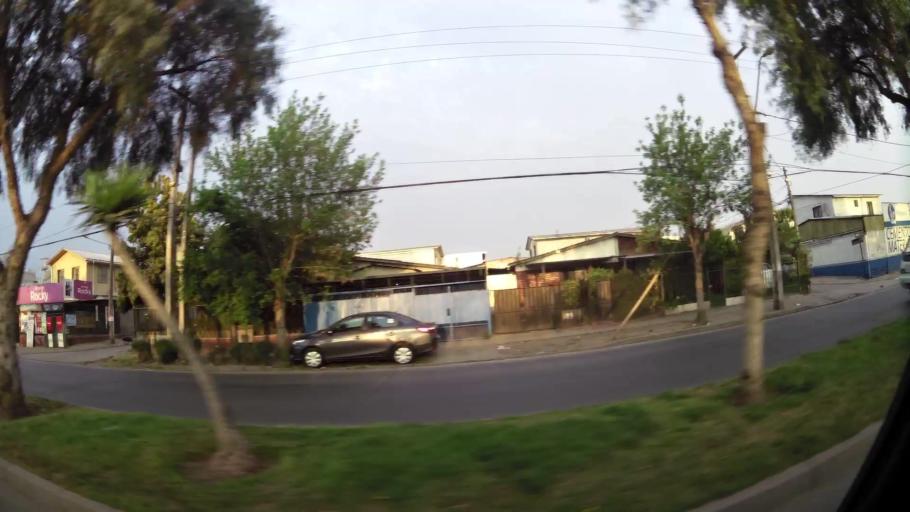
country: CL
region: Santiago Metropolitan
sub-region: Provincia de Santiago
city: Lo Prado
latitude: -33.5094
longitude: -70.7905
